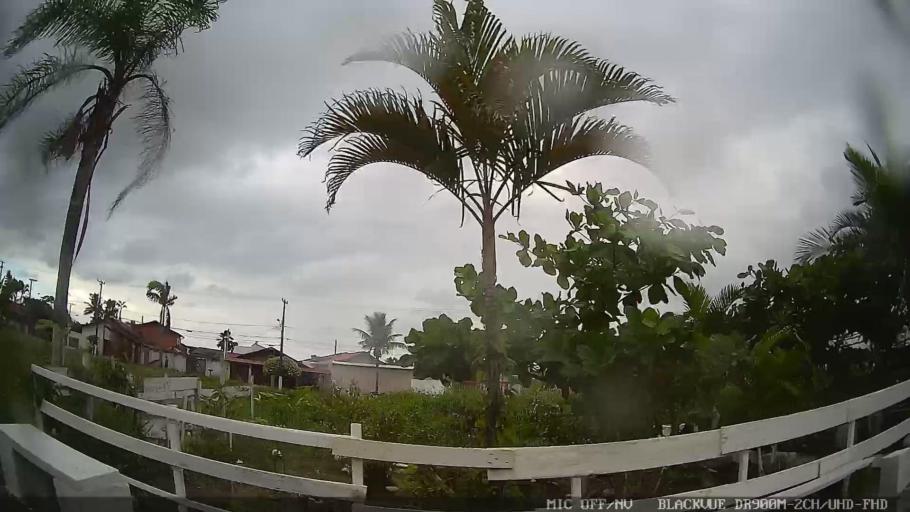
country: BR
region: Sao Paulo
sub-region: Mongagua
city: Mongagua
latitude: -24.1377
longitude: -46.7048
